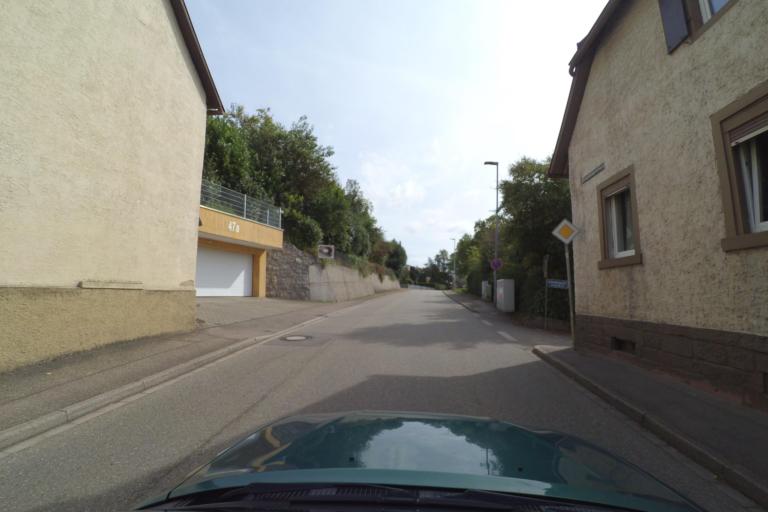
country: DE
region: Baden-Wuerttemberg
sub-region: Freiburg Region
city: Kippenheim
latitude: 48.2914
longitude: 7.8285
